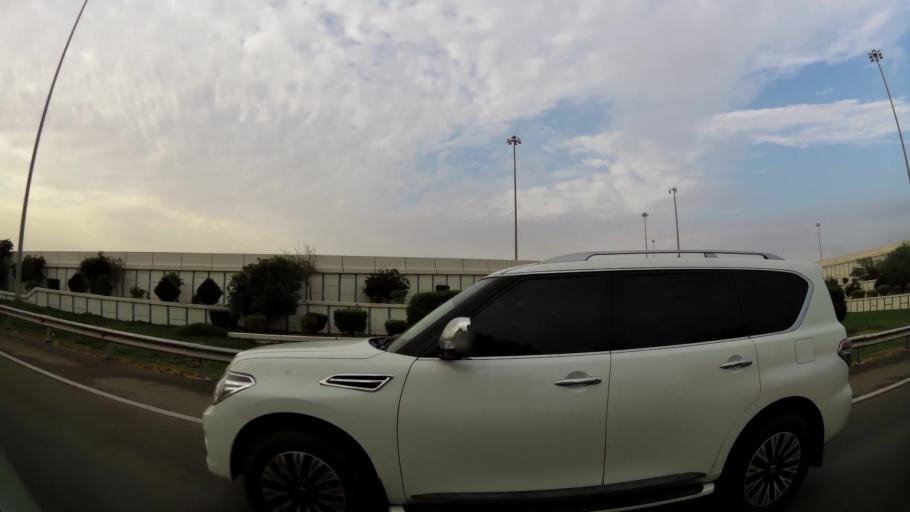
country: AE
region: Abu Dhabi
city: Abu Dhabi
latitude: 24.2804
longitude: 54.6484
